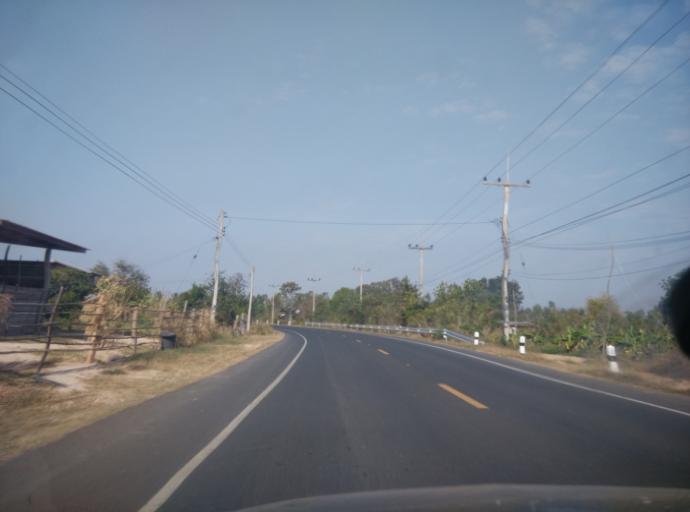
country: TH
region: Sisaket
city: Si Sa Ket
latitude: 15.1165
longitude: 104.2601
